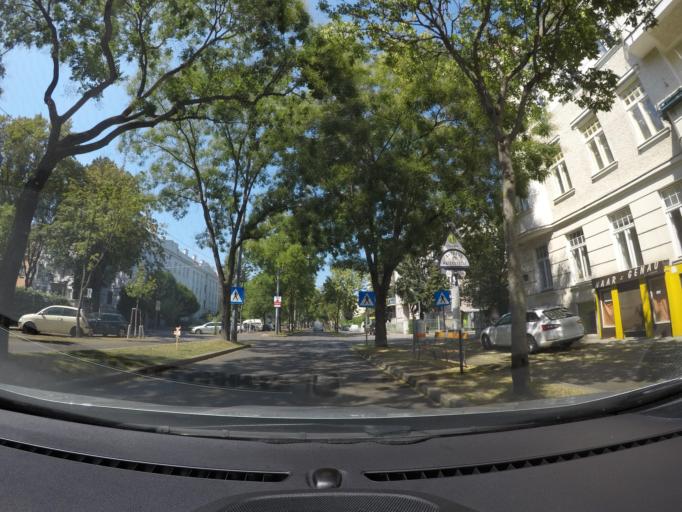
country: AT
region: Lower Austria
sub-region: Politischer Bezirk Modling
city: Perchtoldsdorf
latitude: 48.1876
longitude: 16.2778
